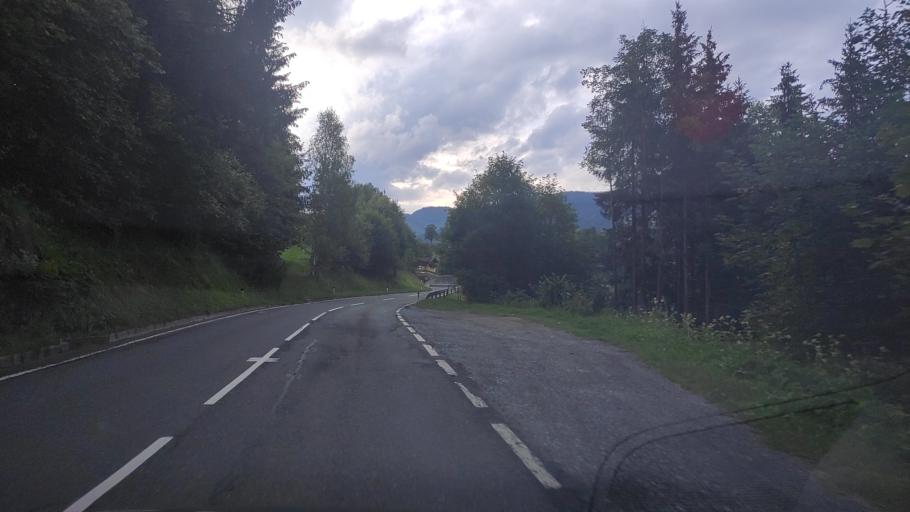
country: AT
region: Salzburg
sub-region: Politischer Bezirk Zell am See
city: Taxenbach
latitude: 47.2803
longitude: 12.9709
